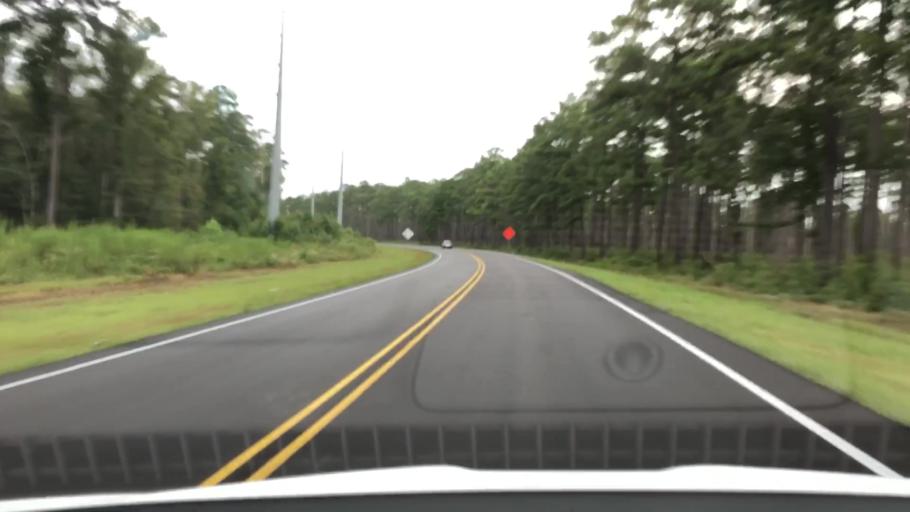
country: US
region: North Carolina
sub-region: Onslow County
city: Swansboro
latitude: 34.7731
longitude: -77.0982
